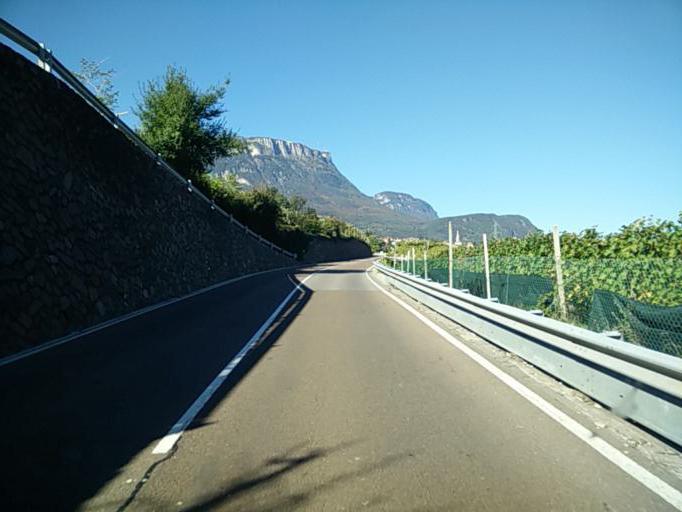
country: IT
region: Trentino-Alto Adige
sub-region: Bolzano
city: Caldaro sulla Strada del Vino
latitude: 46.3978
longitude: 11.2524
